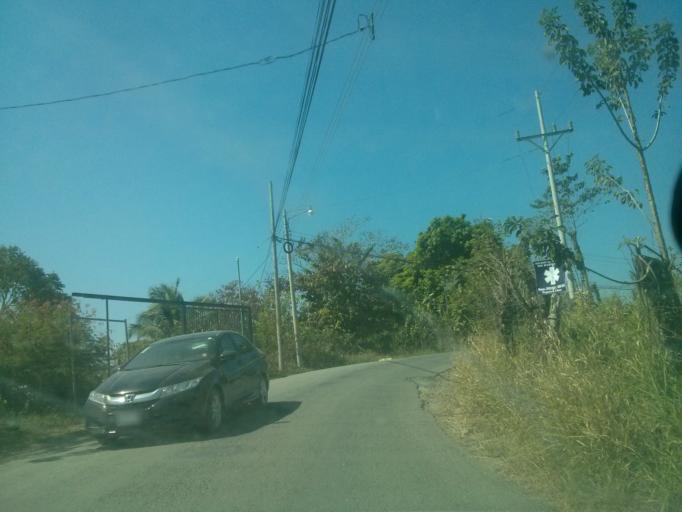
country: CR
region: Puntarenas
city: Paquera
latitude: 9.6758
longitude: -85.1182
